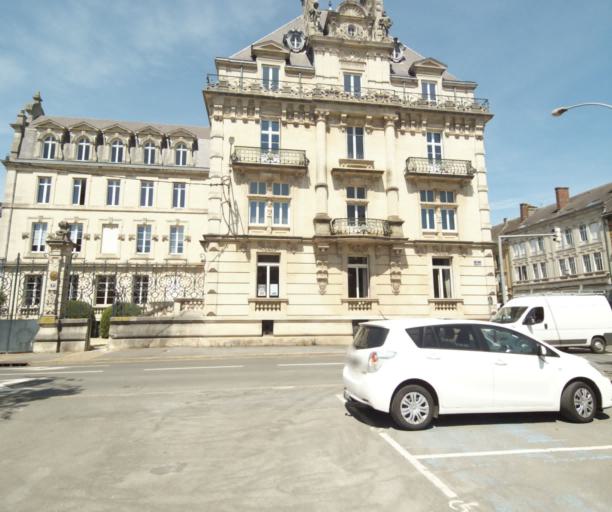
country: FR
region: Champagne-Ardenne
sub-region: Departement des Ardennes
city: Charleville-Mezieres
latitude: 49.7642
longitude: 4.7190
